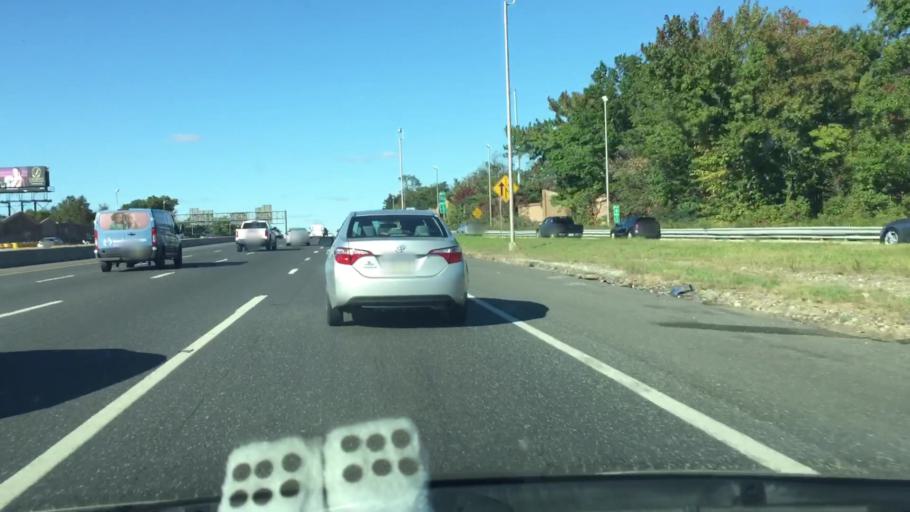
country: US
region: New Jersey
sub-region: Camden County
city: Mount Ephraim
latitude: 39.8764
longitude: -75.1024
